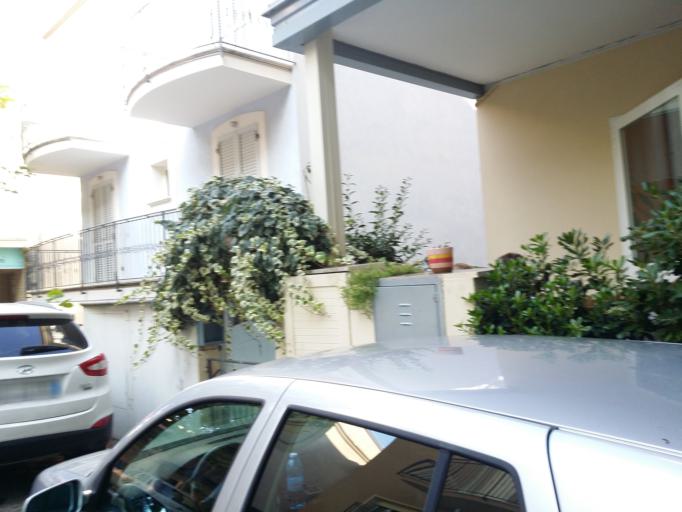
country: IT
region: Emilia-Romagna
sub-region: Provincia di Rimini
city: Rivazzurra
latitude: 44.0344
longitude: 12.6166
